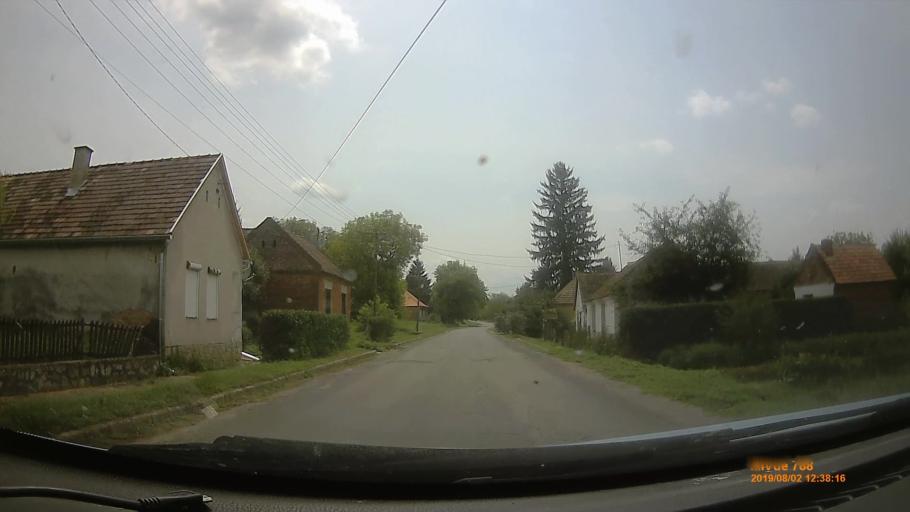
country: HU
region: Baranya
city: Buekkoesd
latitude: 46.0963
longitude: 17.9569
